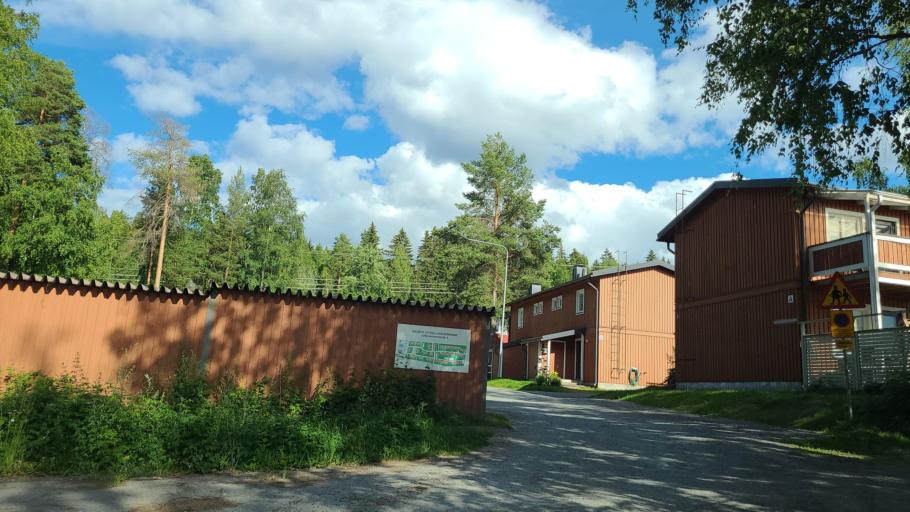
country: FI
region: Northern Savo
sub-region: Kuopio
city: Kuopio
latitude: 62.9253
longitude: 27.6346
